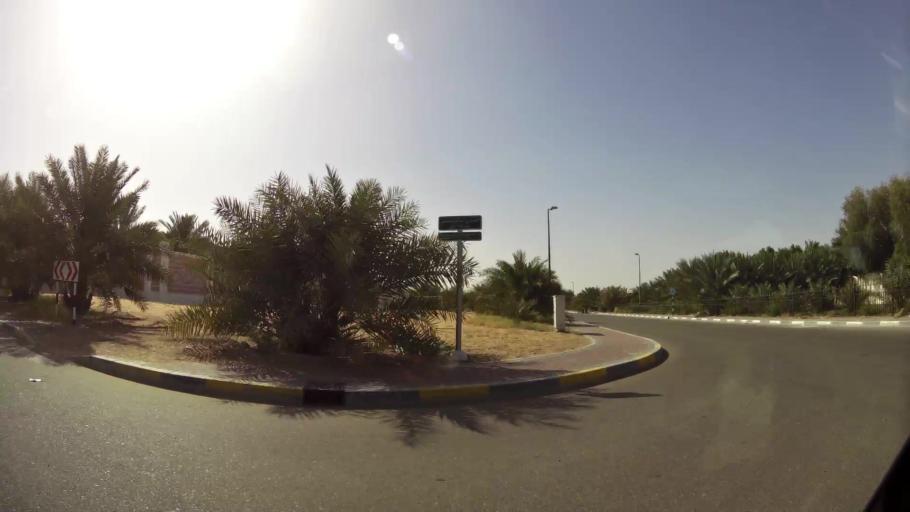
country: OM
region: Al Buraimi
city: Al Buraymi
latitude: 24.3279
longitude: 55.7923
